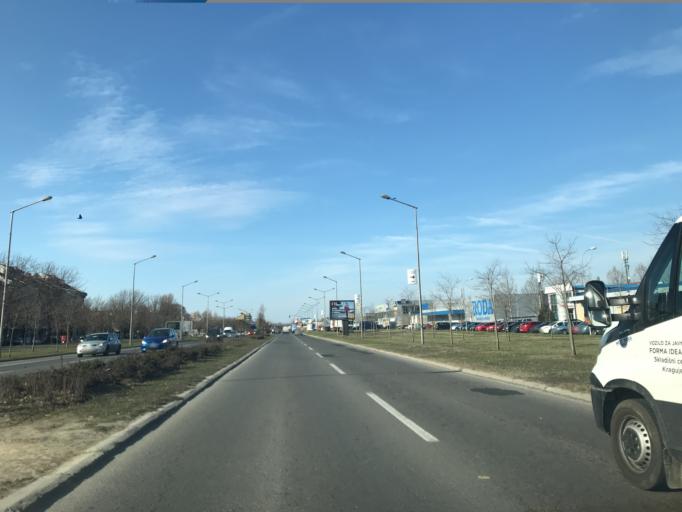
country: RS
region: Autonomna Pokrajina Vojvodina
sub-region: Juznobacki Okrug
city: Novi Sad
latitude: 45.2588
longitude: 19.8041
